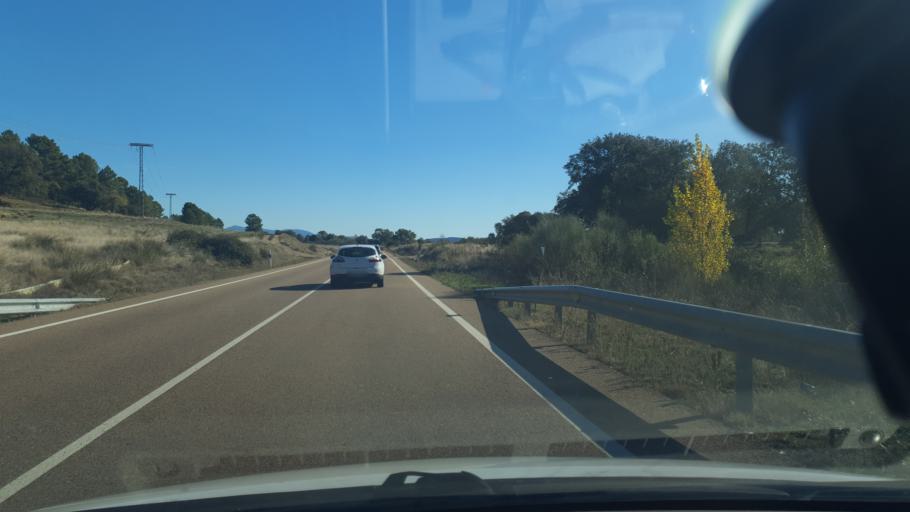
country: ES
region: Castille and Leon
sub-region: Provincia de Avila
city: Poyales del Hoyo
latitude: 40.1629
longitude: -5.1162
